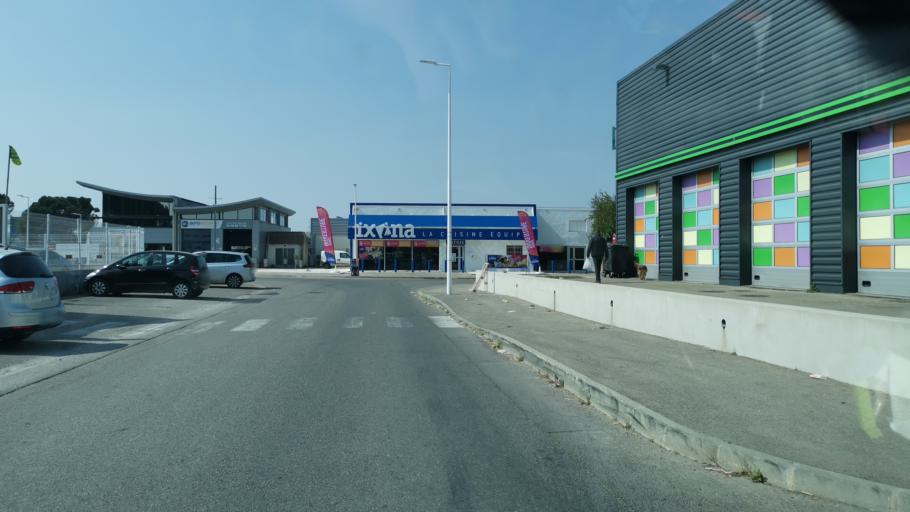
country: FR
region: Provence-Alpes-Cote d'Azur
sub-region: Departement des Bouches-du-Rhone
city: Arles
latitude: 43.6671
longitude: 4.6337
